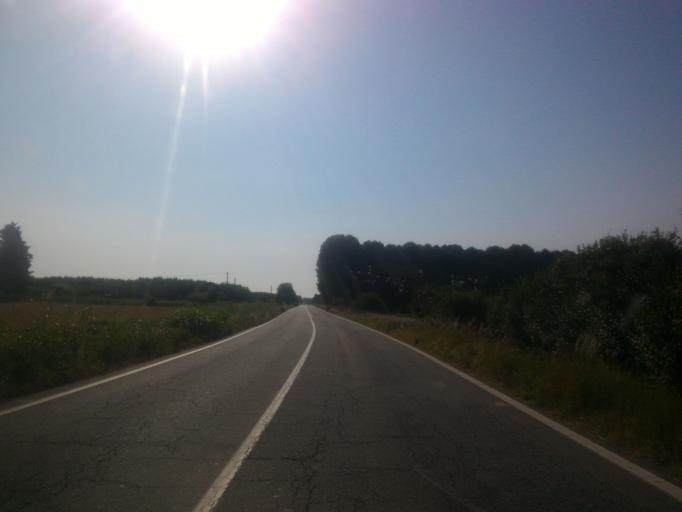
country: IT
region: Piedmont
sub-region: Provincia di Torino
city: Riva
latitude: 44.8765
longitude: 7.3834
